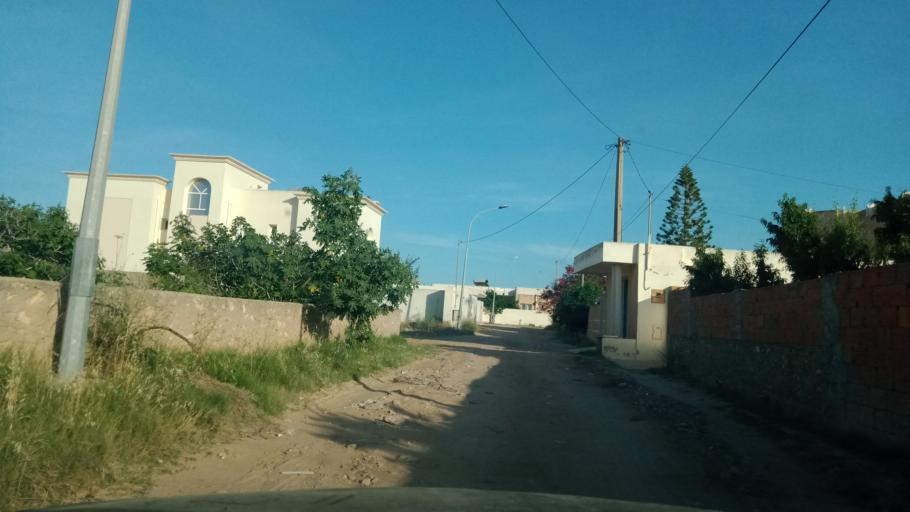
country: TN
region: Safaqis
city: Al Qarmadah
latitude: 34.8148
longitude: 10.7439
